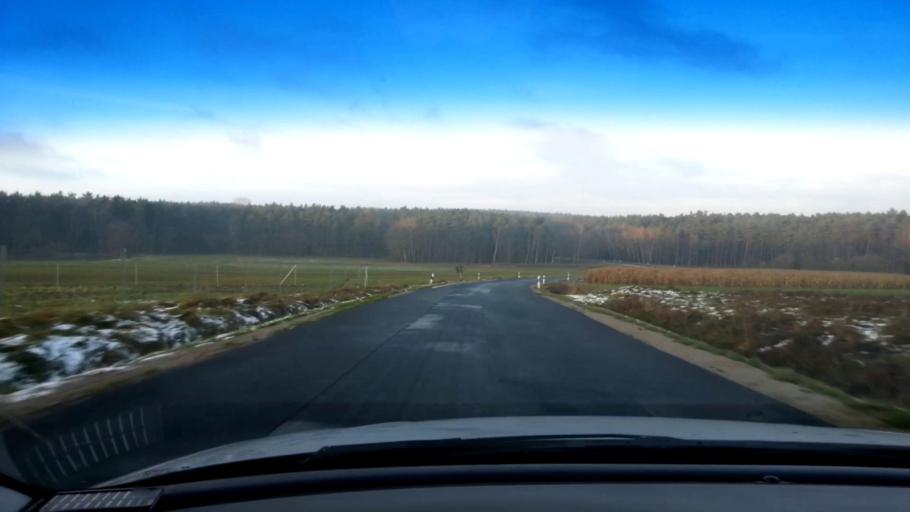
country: DE
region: Bavaria
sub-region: Upper Franconia
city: Frensdorf
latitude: 49.7695
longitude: 10.8938
